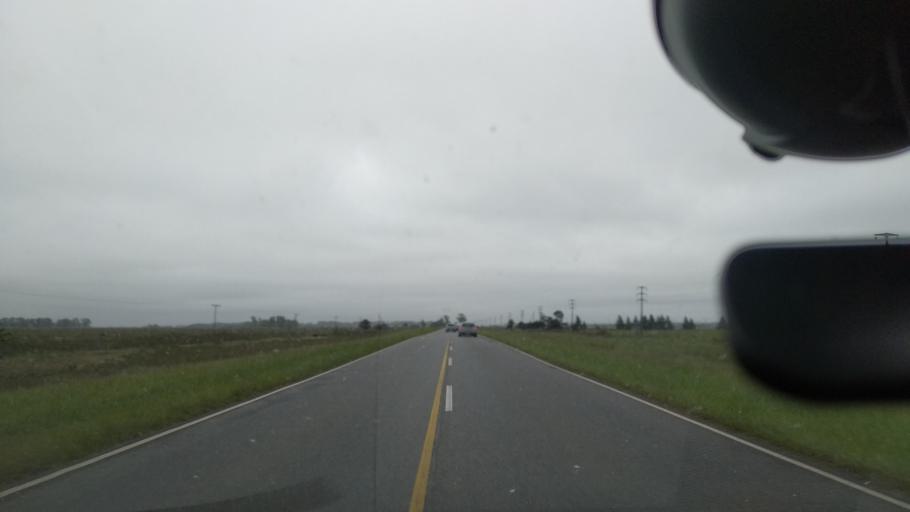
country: AR
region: Buenos Aires
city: Veronica
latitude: -35.3458
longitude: -57.4434
